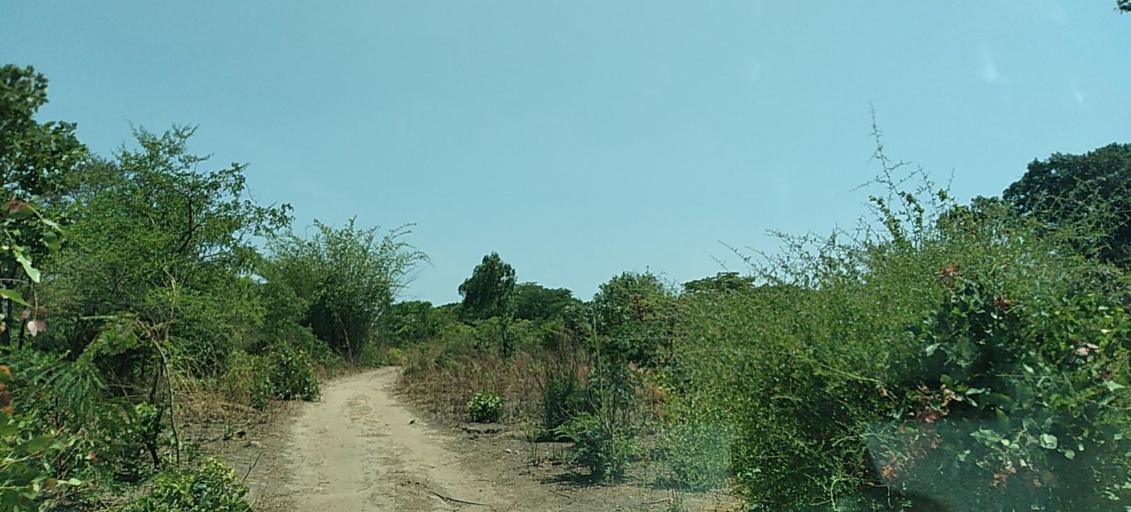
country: ZM
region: Copperbelt
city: Luanshya
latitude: -12.9884
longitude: 28.3283
